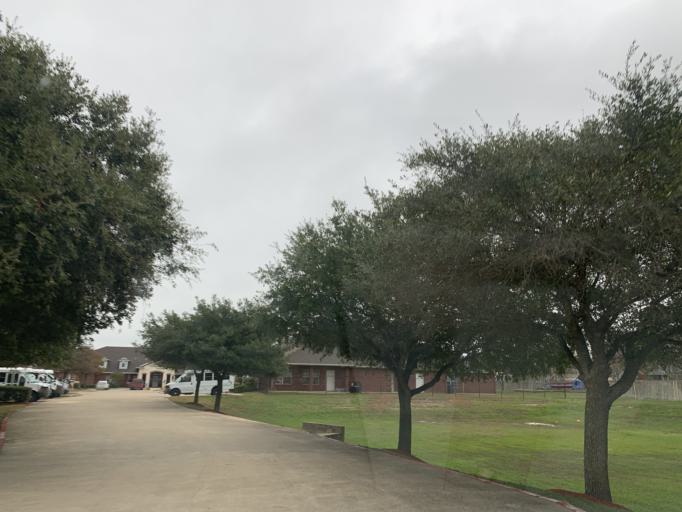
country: US
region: Texas
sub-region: Travis County
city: Windemere
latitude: 30.4962
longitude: -97.6132
